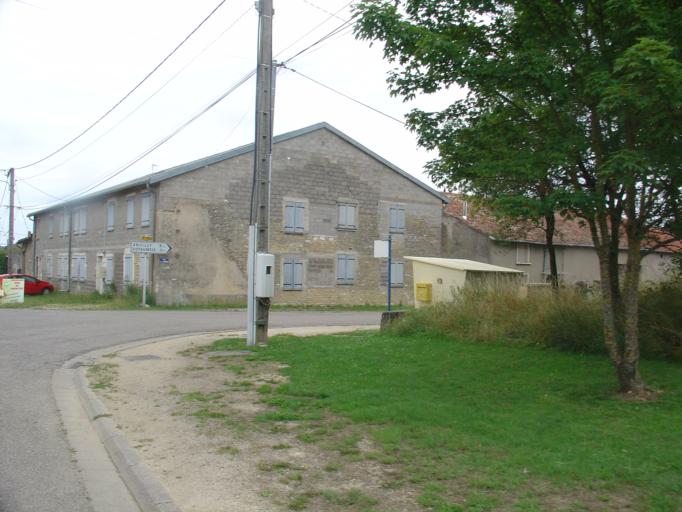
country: FR
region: Lorraine
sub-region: Departement de Meurthe-et-Moselle
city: Villey-Saint-Etienne
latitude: 48.8170
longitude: 5.8903
